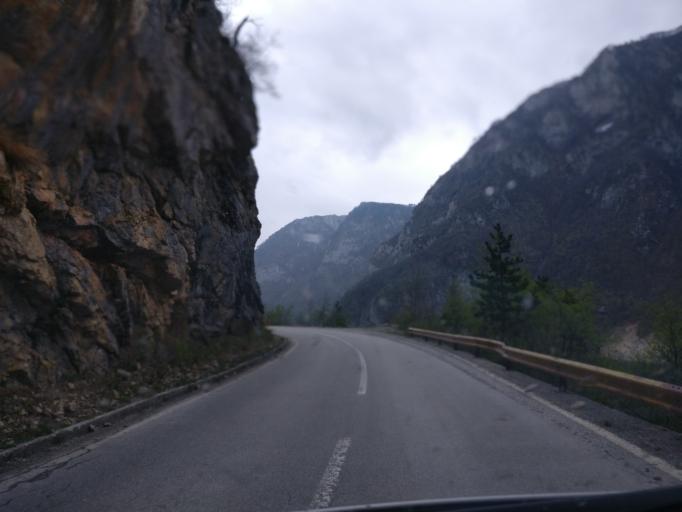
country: ME
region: Opstina Pluzine
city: Pluzine
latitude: 43.2412
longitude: 18.8409
